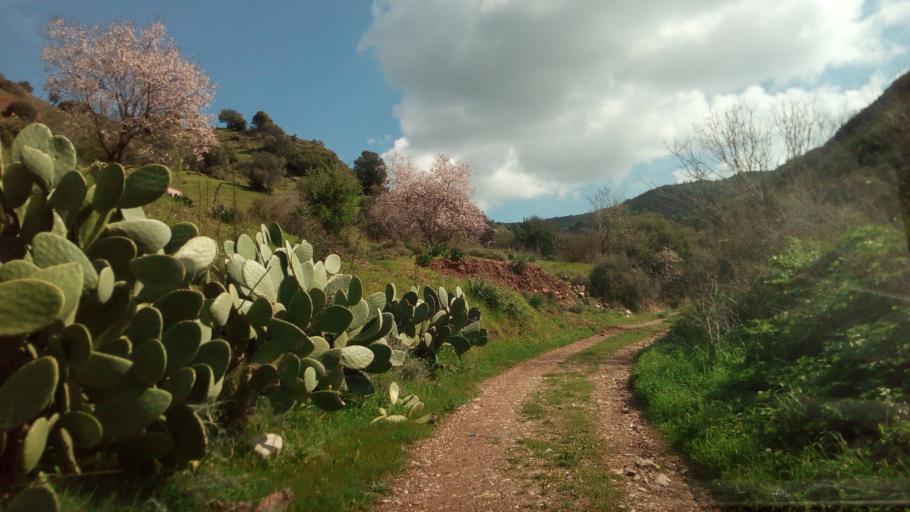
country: CY
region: Pafos
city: Mesogi
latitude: 34.8059
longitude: 32.5357
